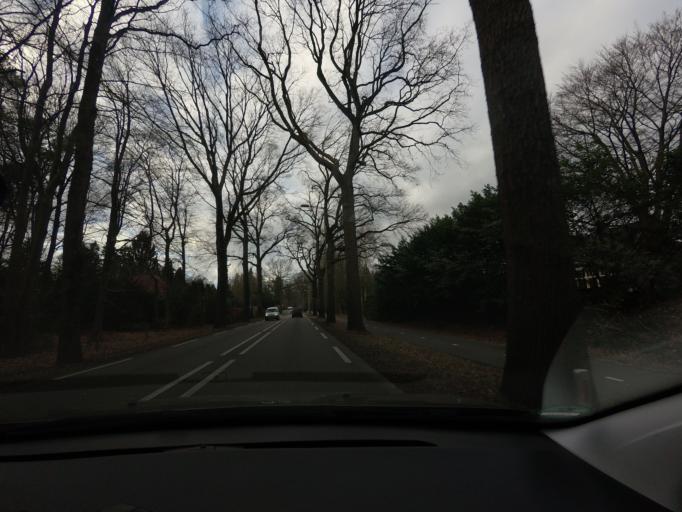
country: NL
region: Gelderland
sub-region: Gemeente Lochem
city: Eefde
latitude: 52.1814
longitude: 6.2156
